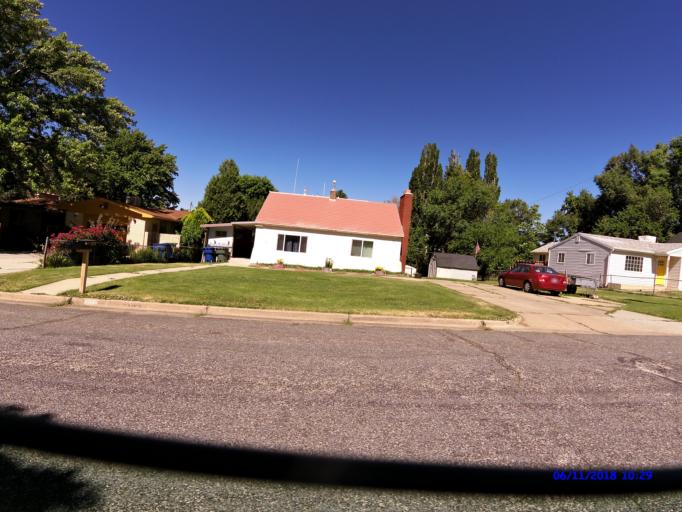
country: US
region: Utah
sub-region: Weber County
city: Ogden
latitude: 41.2274
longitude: -111.9424
